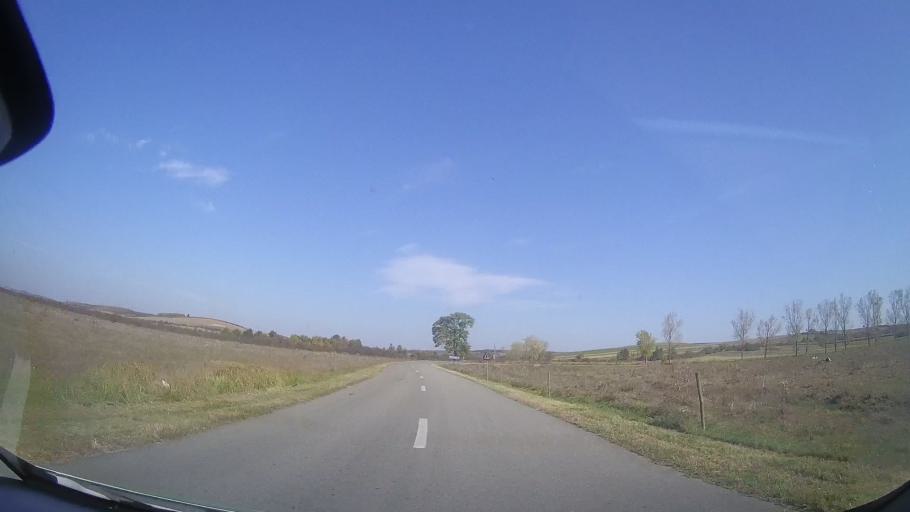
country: RO
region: Timis
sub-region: Comuna Ghizela
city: Ghizela
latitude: 45.8226
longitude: 21.7270
